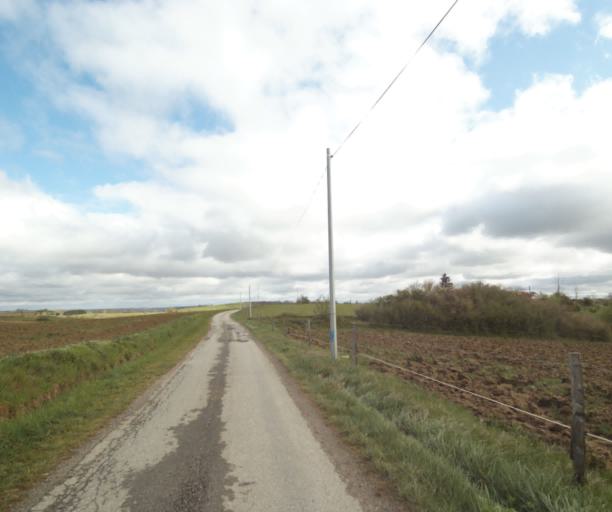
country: FR
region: Midi-Pyrenees
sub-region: Departement de l'Ariege
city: Saverdun
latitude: 43.1974
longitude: 1.5401
